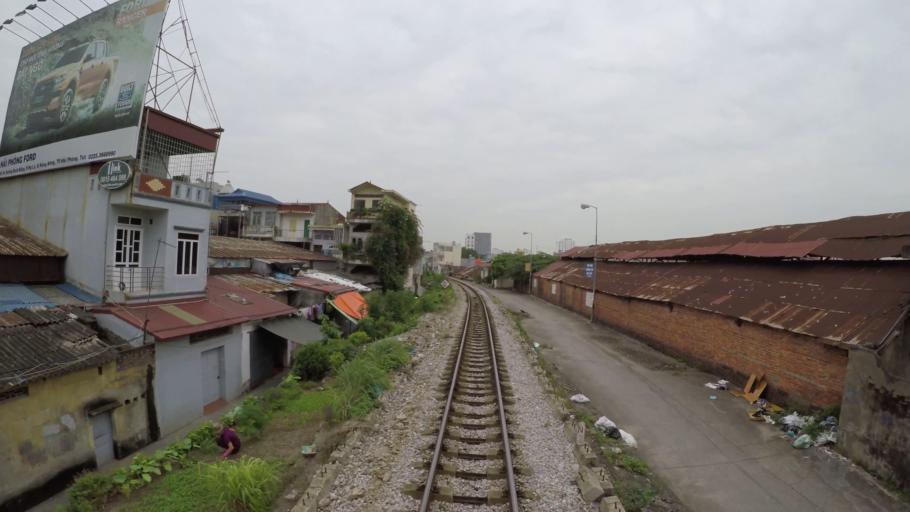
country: VN
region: Hai Phong
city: Haiphong
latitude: 20.8704
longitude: 106.6527
